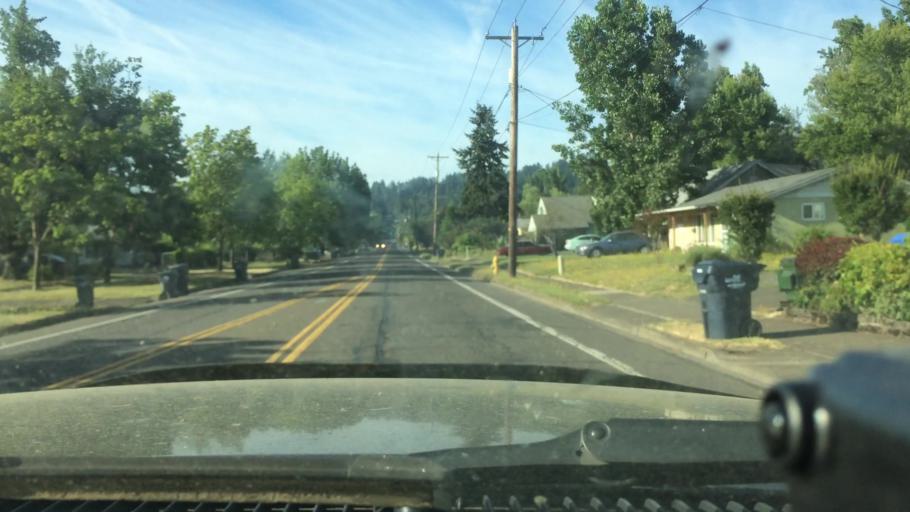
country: US
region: Oregon
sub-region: Lane County
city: Eugene
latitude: 44.0387
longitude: -123.1179
